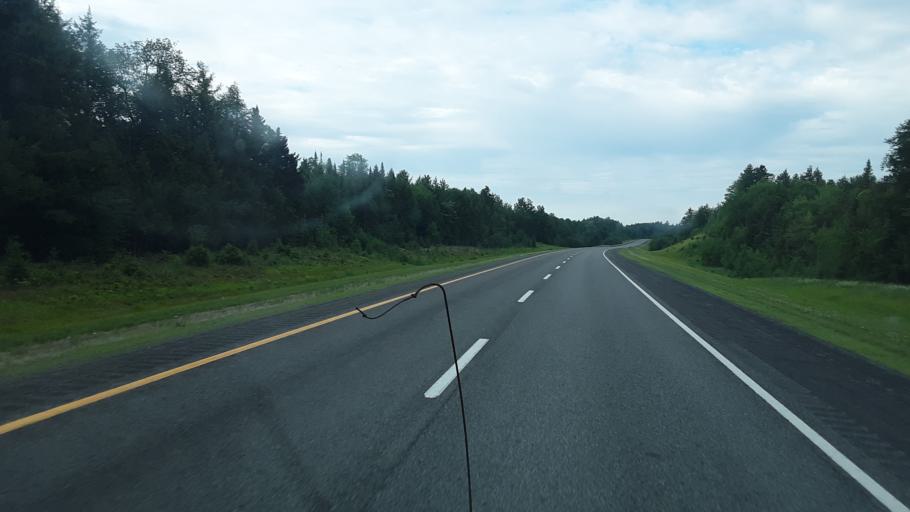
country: US
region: Maine
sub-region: Penobscot County
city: Medway
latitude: 45.6901
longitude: -68.4888
